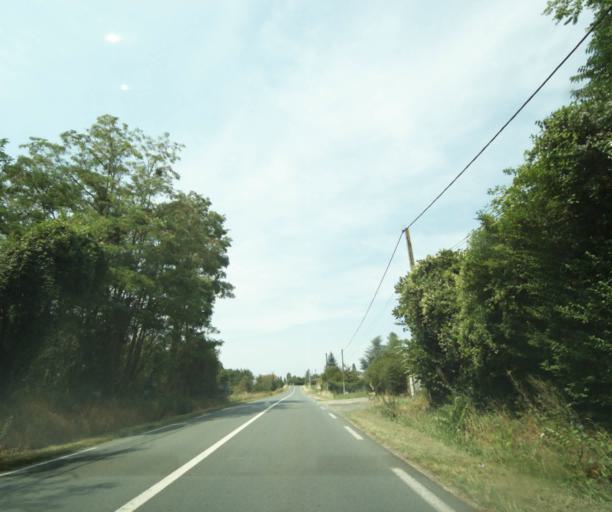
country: FR
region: Poitou-Charentes
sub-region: Departement de la Vienne
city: Vouneuil-sur-Vienne
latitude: 46.7172
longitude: 0.5550
